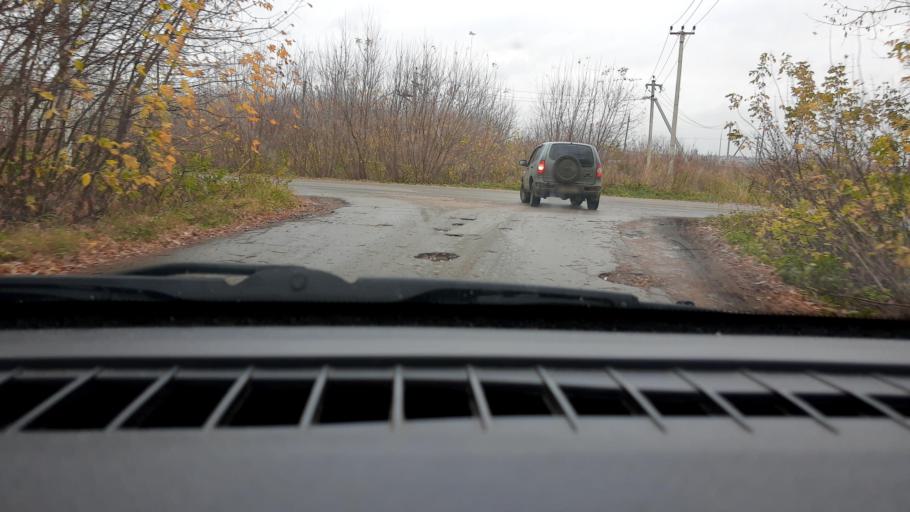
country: RU
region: Nizjnij Novgorod
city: Afonino
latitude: 56.2129
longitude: 44.1041
